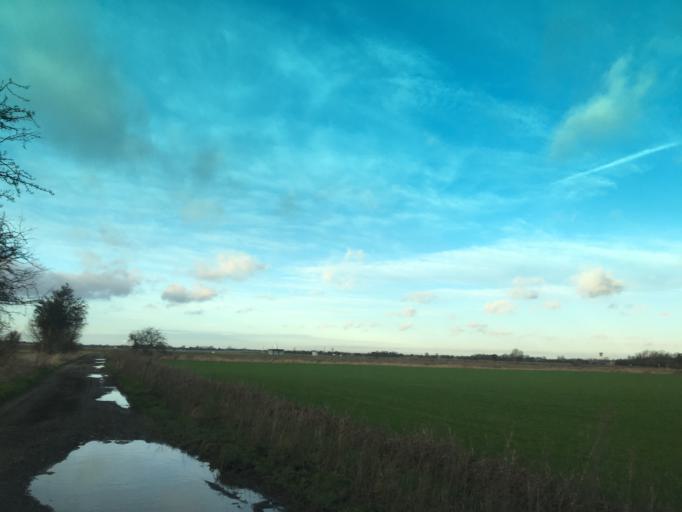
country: DK
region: Capital Region
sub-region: Tarnby Kommune
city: Tarnby
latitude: 55.5875
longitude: 12.6121
